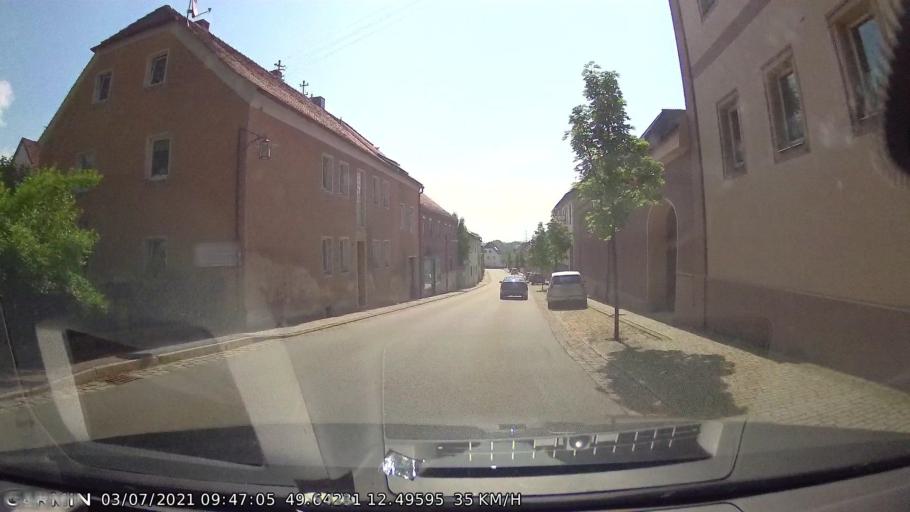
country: DE
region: Bavaria
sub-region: Upper Palatinate
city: Waidhaus
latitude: 49.6422
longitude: 12.4960
